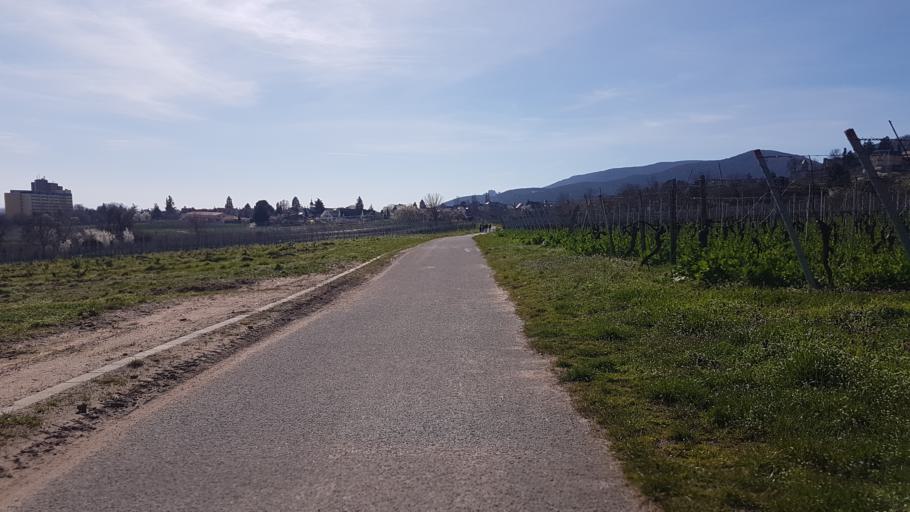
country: DE
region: Rheinland-Pfalz
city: Neustadt
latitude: 49.3660
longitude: 8.1436
